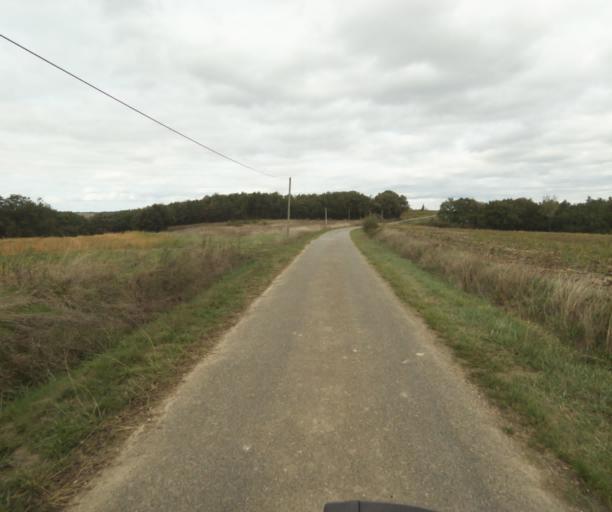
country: FR
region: Midi-Pyrenees
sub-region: Departement du Tarn-et-Garonne
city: Beaumont-de-Lomagne
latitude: 43.8422
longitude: 1.0952
